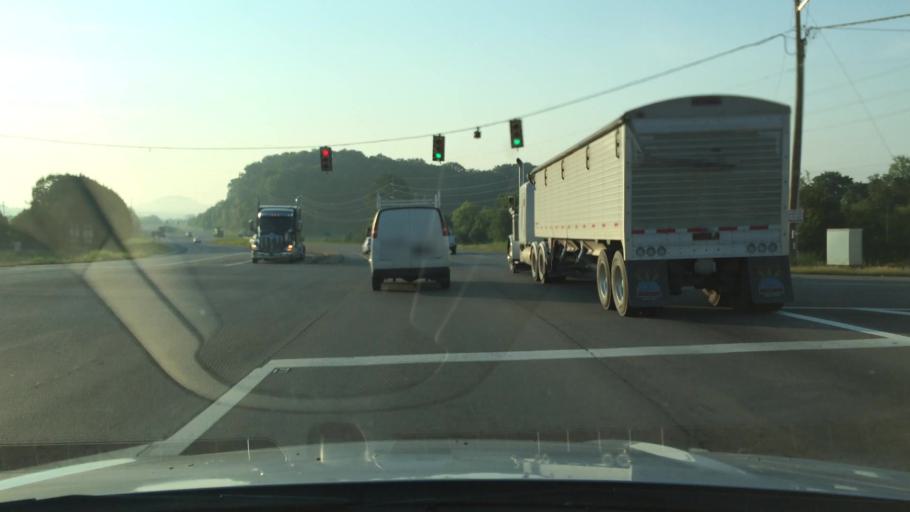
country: US
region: Tennessee
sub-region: Giles County
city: Pulaski
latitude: 35.1709
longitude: -87.0553
